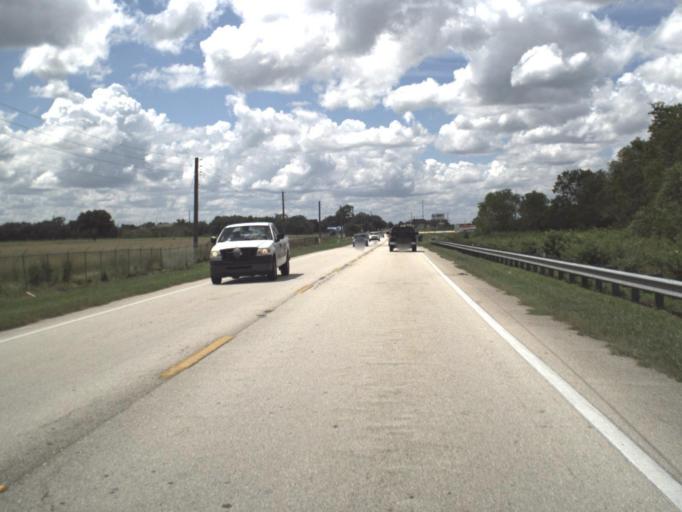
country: US
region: Florida
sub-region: Polk County
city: Dundee
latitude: 28.0188
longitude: -81.6494
